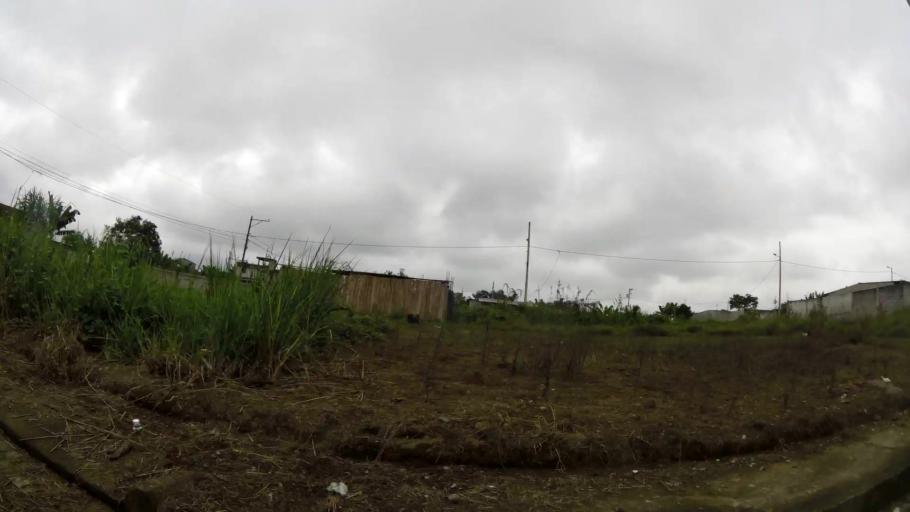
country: EC
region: Santo Domingo de los Tsachilas
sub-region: Canton Santo Domingo de los Colorados
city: Santo Domingo de los Colorados
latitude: -0.2803
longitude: -79.1895
